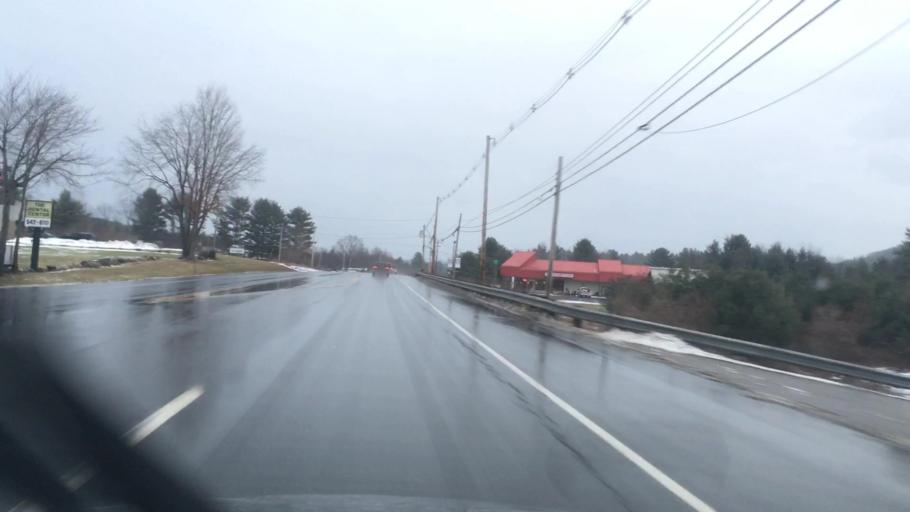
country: US
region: New Hampshire
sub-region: Sullivan County
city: Unity
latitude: 43.3674
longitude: -72.2582
